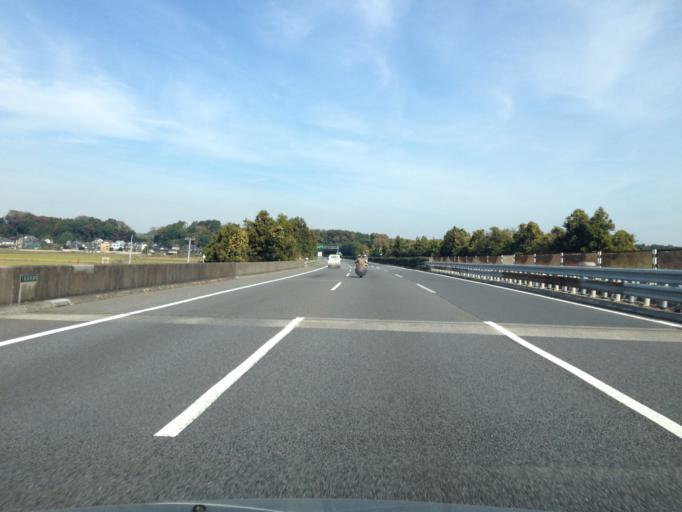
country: JP
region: Ibaraki
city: Naka
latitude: 36.0991
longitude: 140.1713
